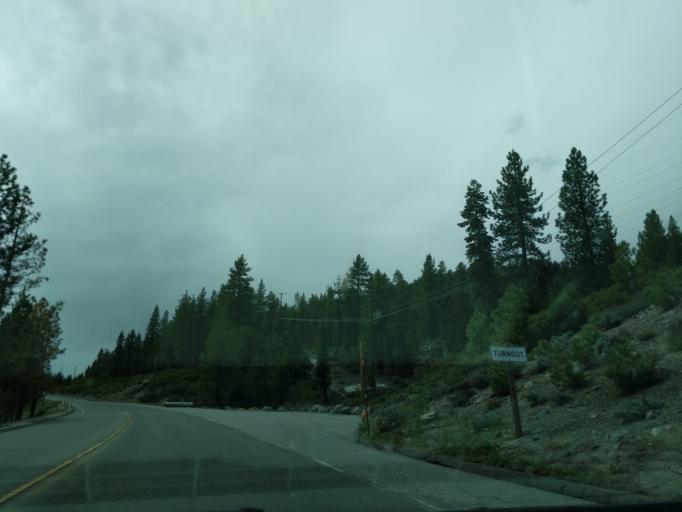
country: US
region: California
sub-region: Placer County
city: Tahoe Vista
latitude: 39.2580
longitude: -120.0505
